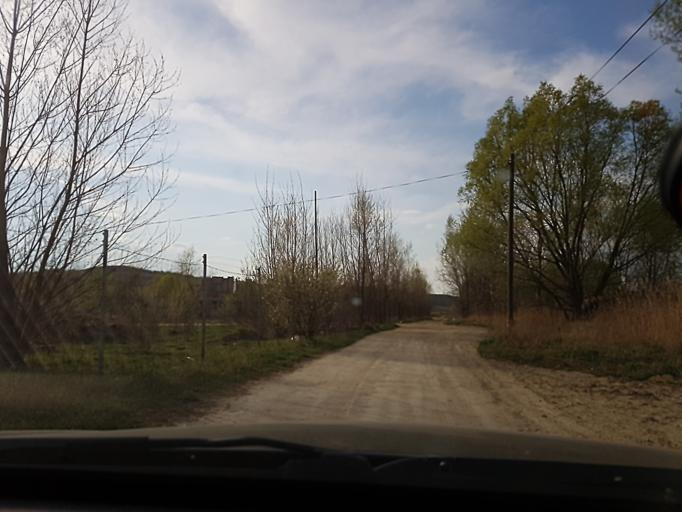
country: HU
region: Pest
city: Piliscsaba
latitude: 47.6340
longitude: 18.8148
